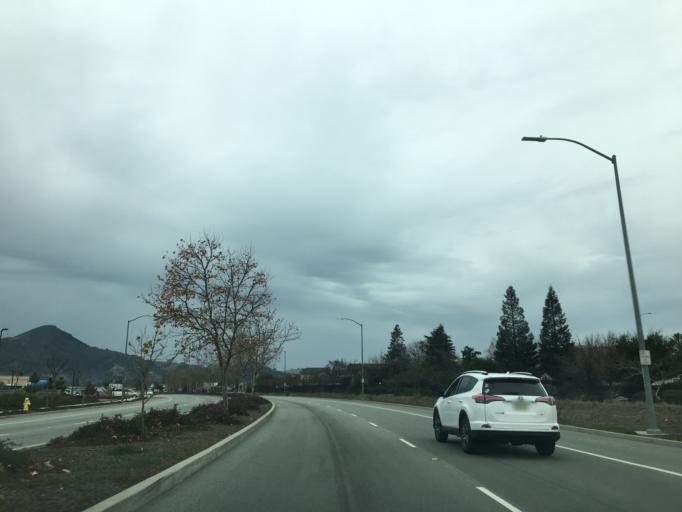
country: US
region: California
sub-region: Santa Clara County
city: Morgan Hill
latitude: 37.1222
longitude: -121.6365
